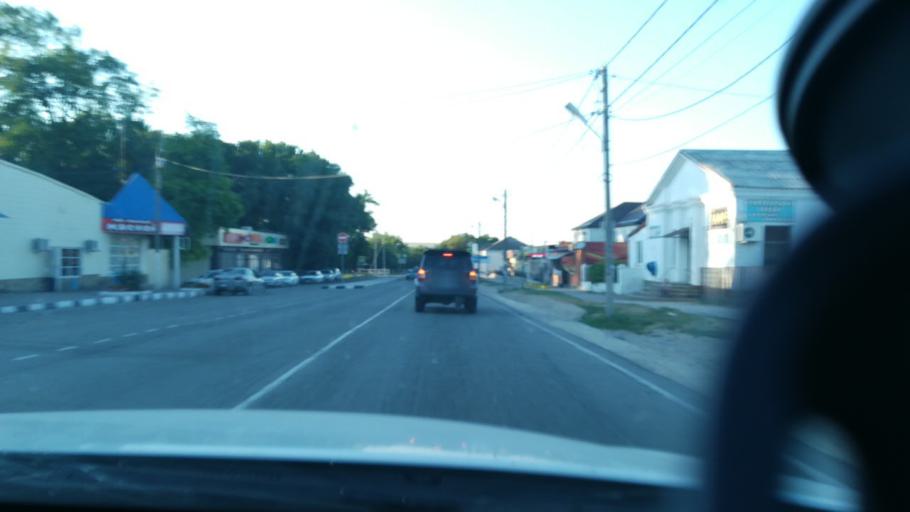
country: RU
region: Krasnodarskiy
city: Gostagayevskaya
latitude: 45.0242
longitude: 37.5031
